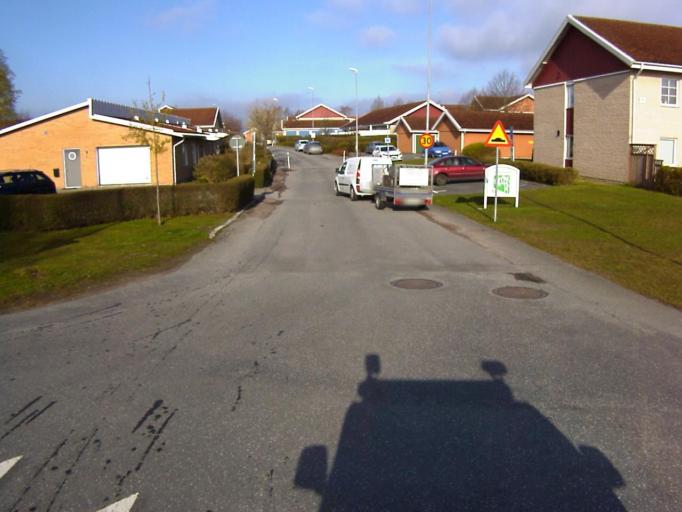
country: SE
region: Skane
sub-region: Kristianstads Kommun
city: Kristianstad
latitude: 56.0158
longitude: 14.1057
